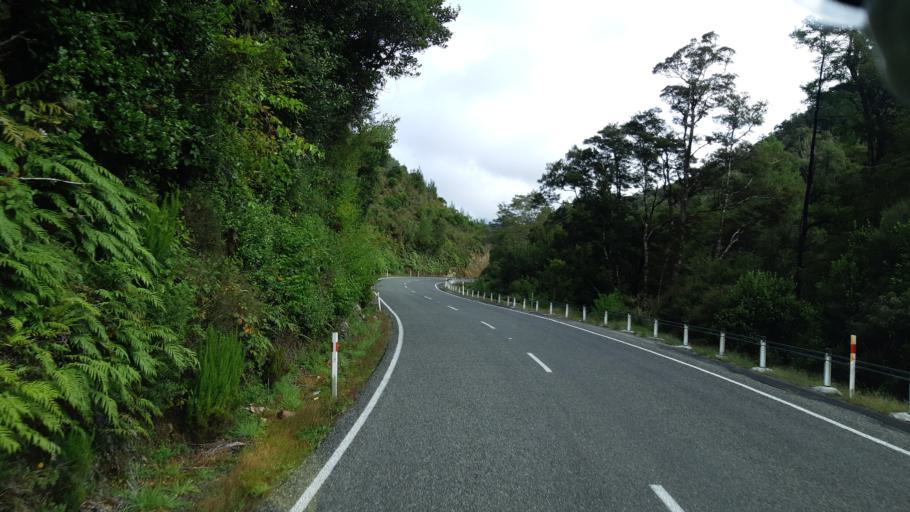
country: NZ
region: West Coast
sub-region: Buller District
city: Westport
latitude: -41.9874
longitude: 172.2108
